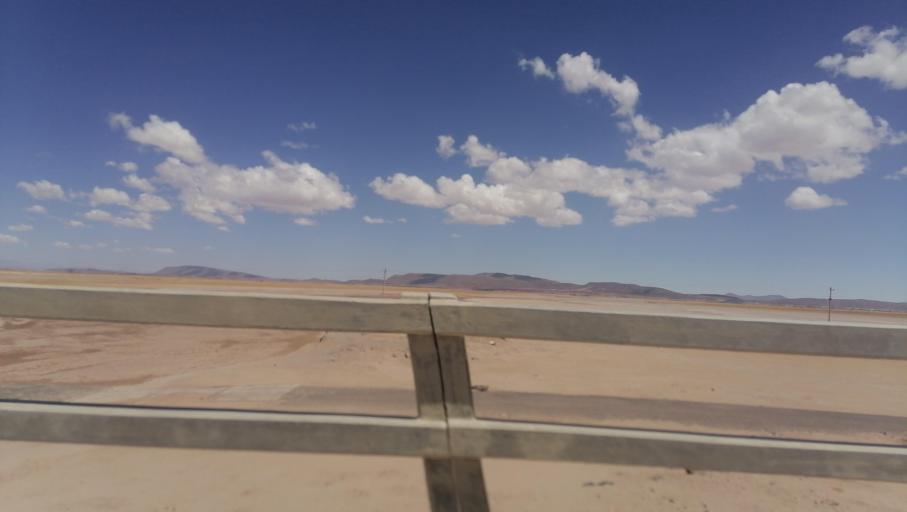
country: BO
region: Oruro
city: Challapata
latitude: -19.2136
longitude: -67.0251
